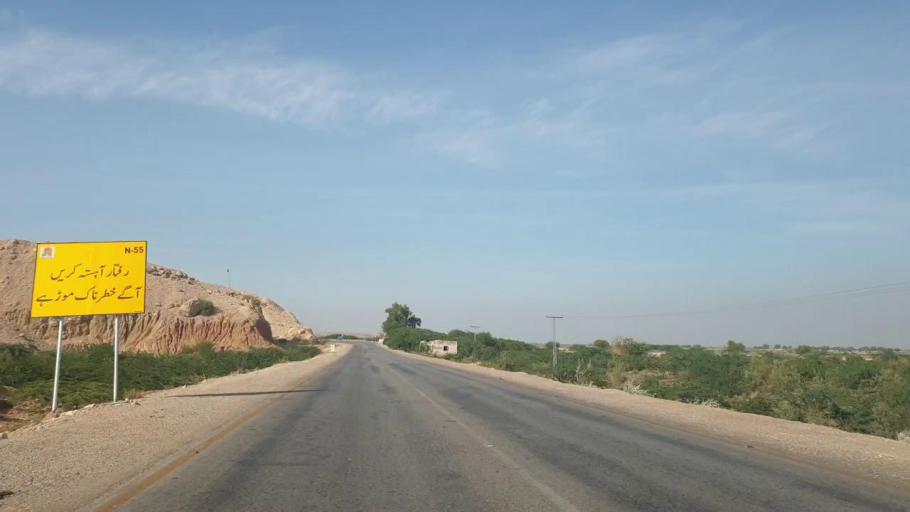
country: PK
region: Sindh
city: Sehwan
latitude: 26.3183
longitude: 67.8887
